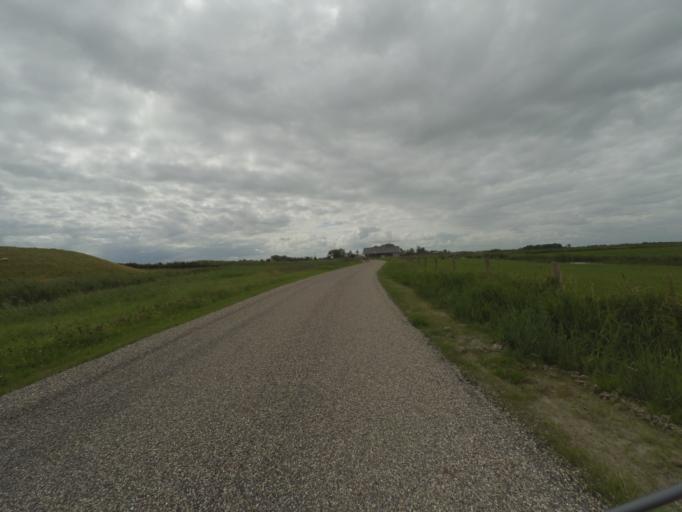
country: NL
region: Friesland
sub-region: Gemeente Dongeradeel
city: Anjum
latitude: 53.3533
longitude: 6.1429
